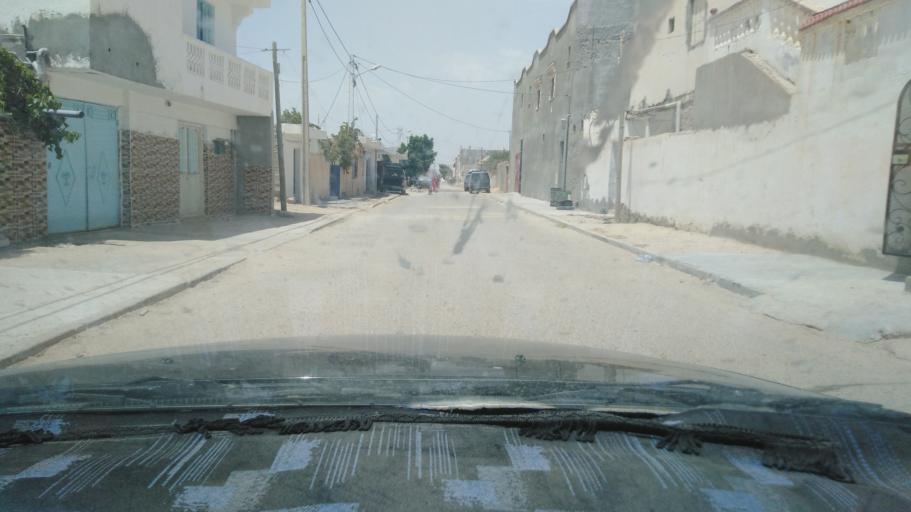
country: TN
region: Qabis
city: Matmata
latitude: 33.6179
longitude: 10.2726
